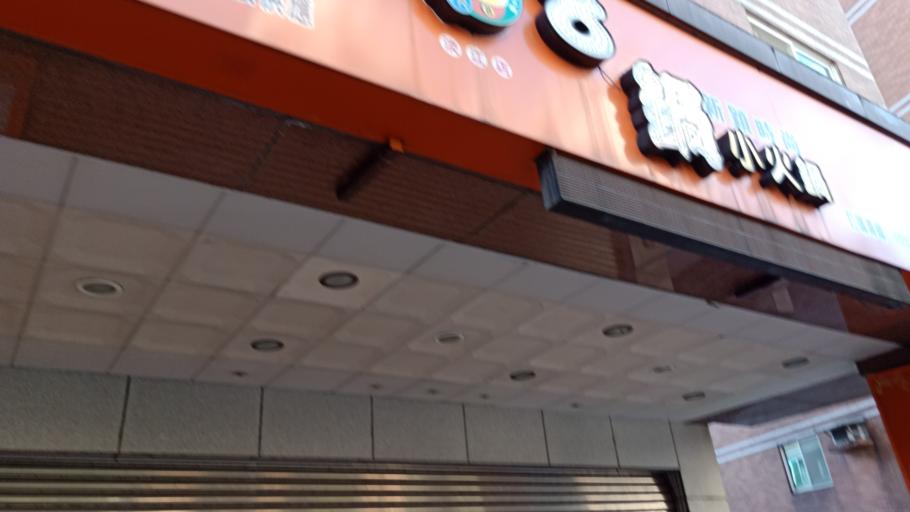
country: TW
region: Taipei
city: Taipei
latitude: 25.1775
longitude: 121.4482
